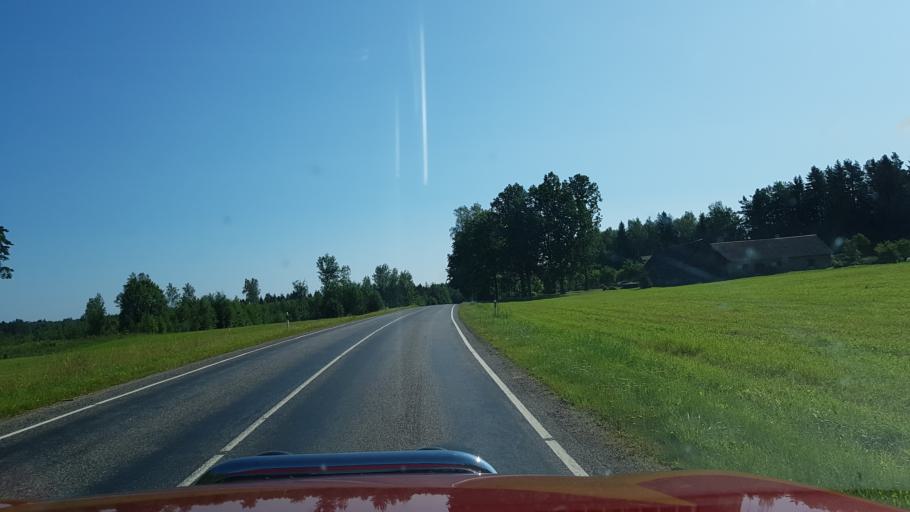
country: EE
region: Polvamaa
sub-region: Polva linn
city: Polva
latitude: 57.9867
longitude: 26.8874
